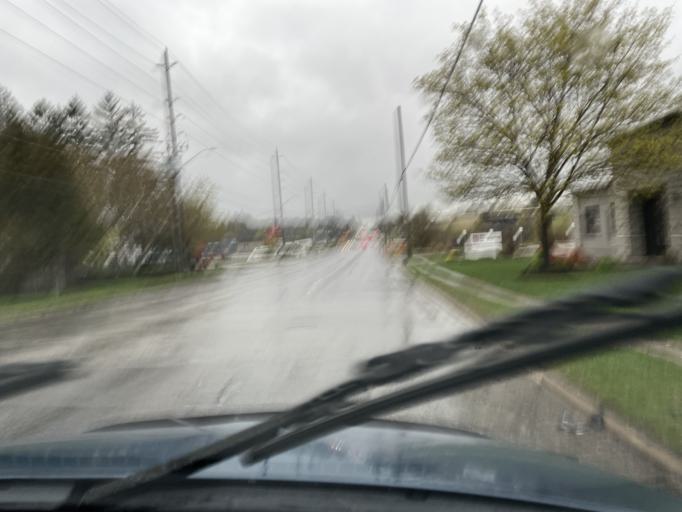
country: CA
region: Ontario
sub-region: Wellington County
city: Guelph
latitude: 43.5537
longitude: -80.2262
